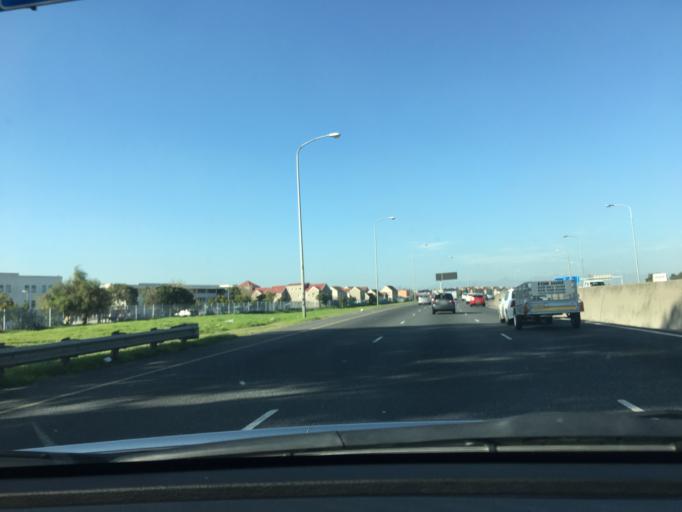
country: ZA
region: Western Cape
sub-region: City of Cape Town
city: Lansdowne
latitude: -33.9502
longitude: 18.5242
